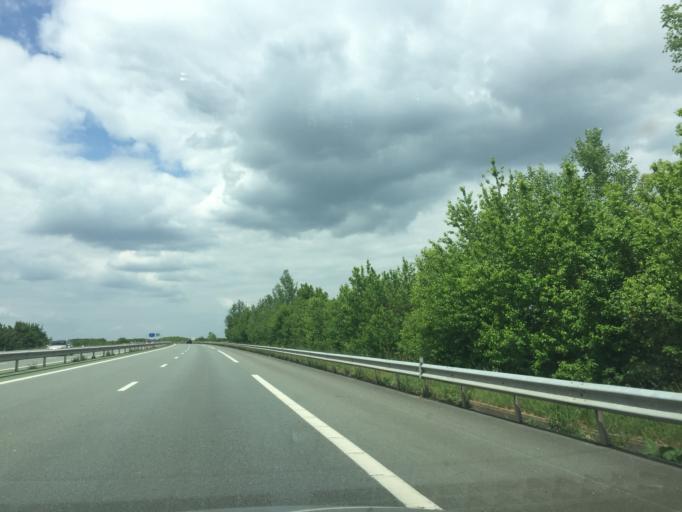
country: FR
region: Poitou-Charentes
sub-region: Departement des Deux-Sevres
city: Saint-Gelais
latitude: 46.4085
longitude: -0.3885
